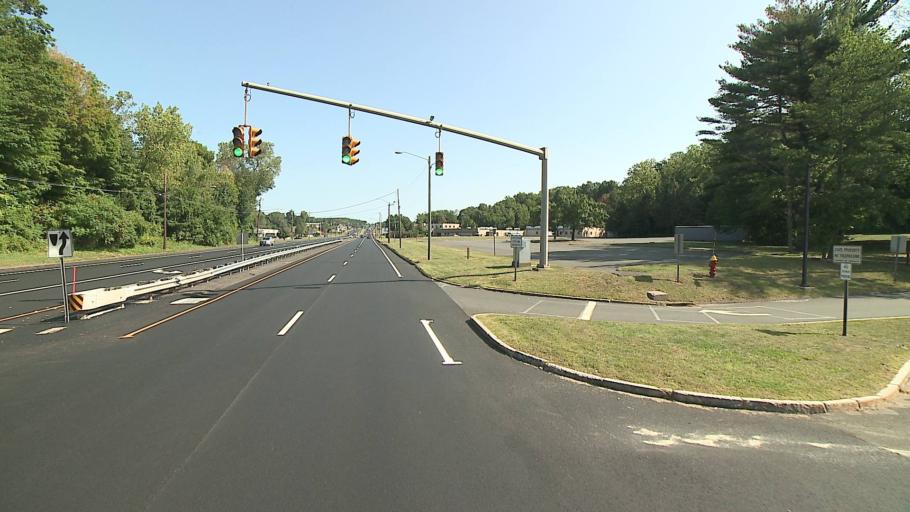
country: US
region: Connecticut
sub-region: Hartford County
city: Newington
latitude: 41.6749
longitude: -72.7148
